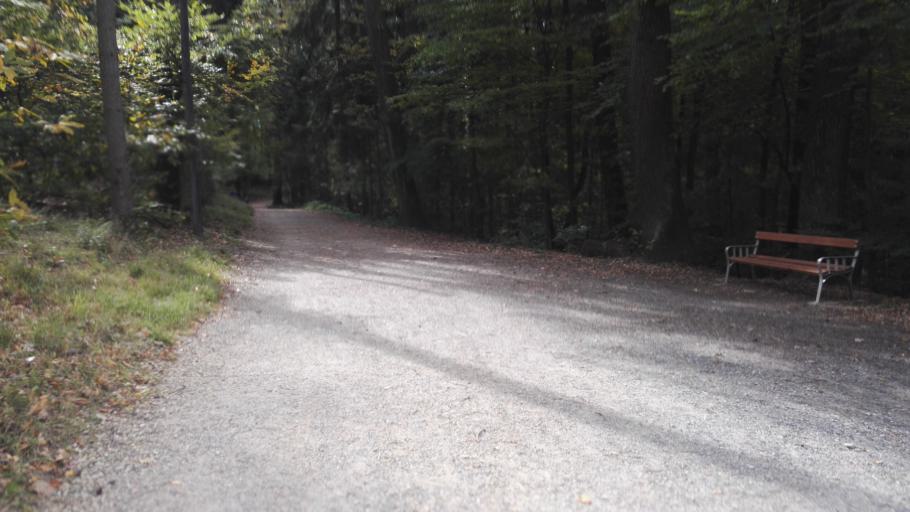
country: AT
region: Styria
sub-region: Graz Stadt
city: Mariatrost
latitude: 47.0946
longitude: 15.4727
